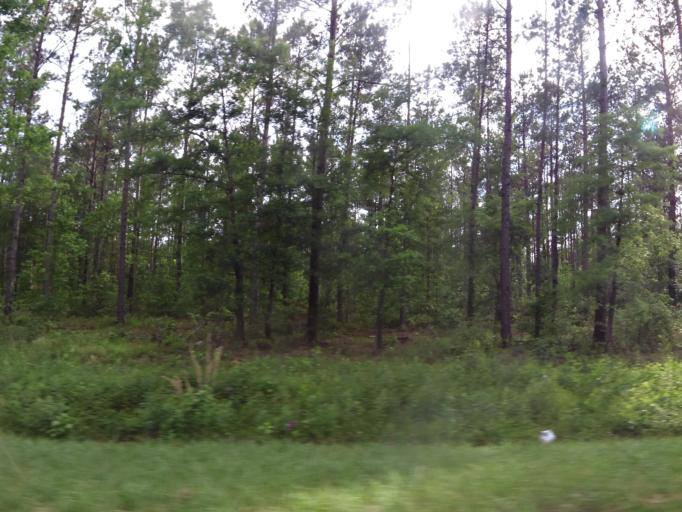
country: US
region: South Carolina
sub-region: Jasper County
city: Ridgeland
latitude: 32.5583
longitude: -81.1732
